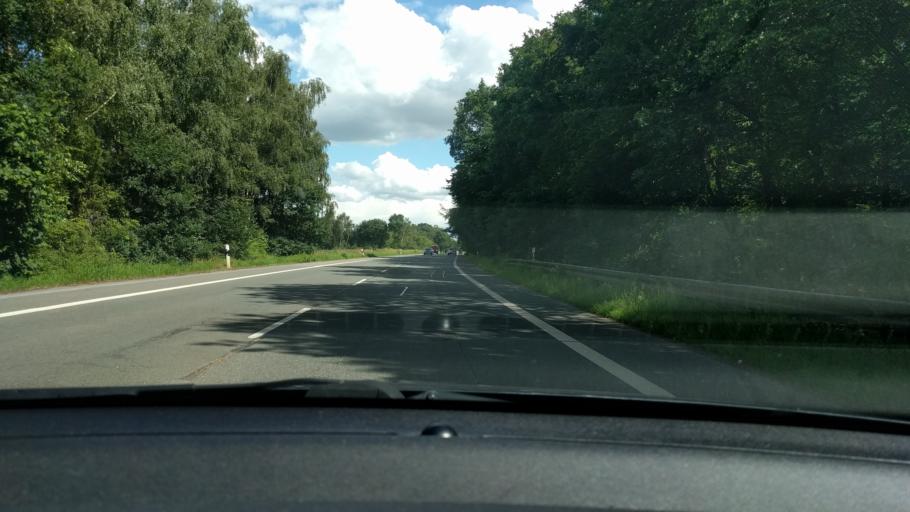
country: DE
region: North Rhine-Westphalia
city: Oer-Erkenschwick
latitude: 51.7133
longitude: 7.2786
